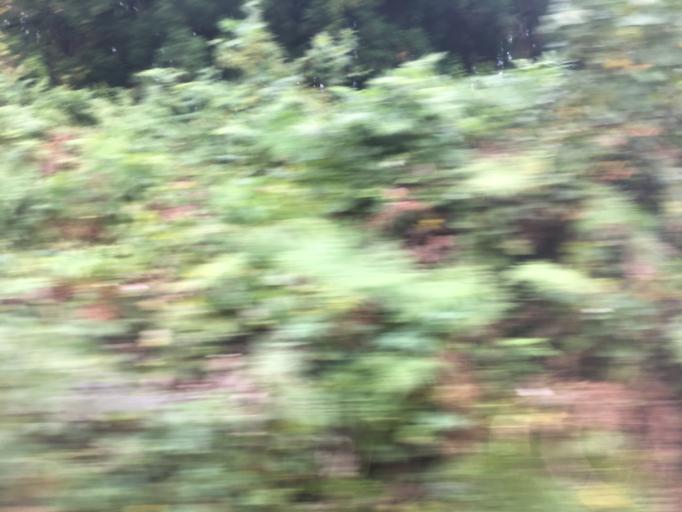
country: JP
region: Niigata
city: Murakami
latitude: 38.0616
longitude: 139.6706
